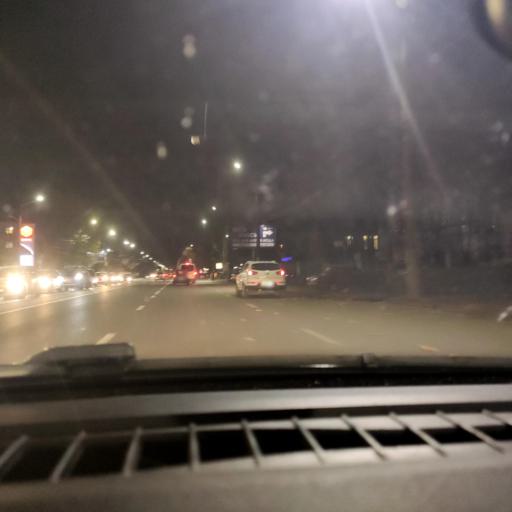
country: RU
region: Voronezj
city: Voronezh
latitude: 51.6769
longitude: 39.1712
